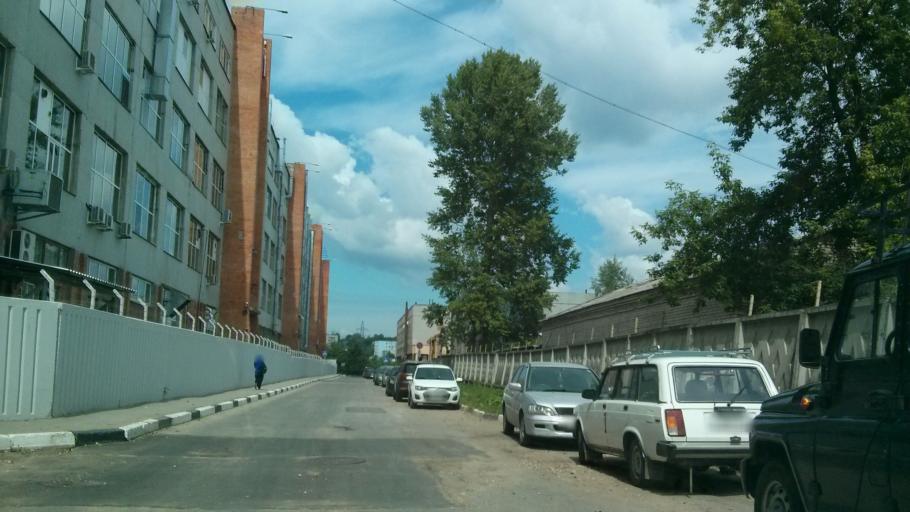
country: RU
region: Nizjnij Novgorod
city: Nizhniy Novgorod
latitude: 56.3013
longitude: 44.0178
